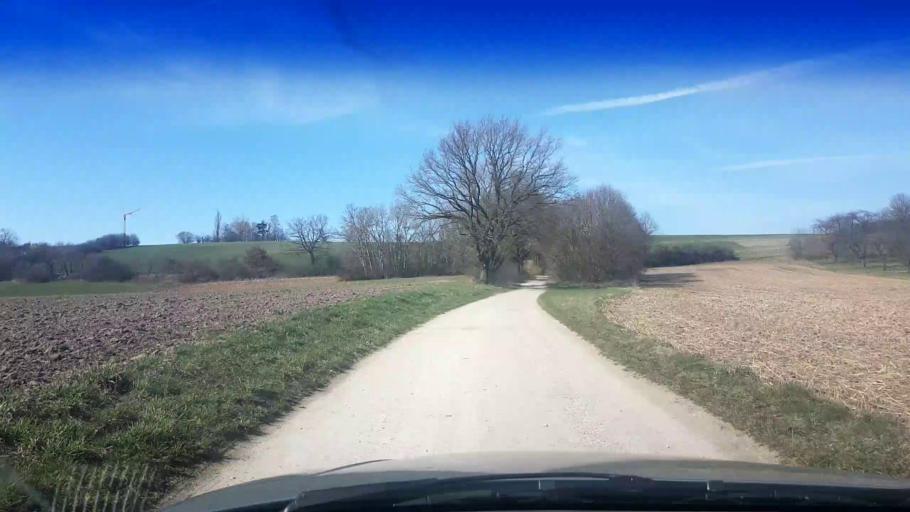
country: DE
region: Bavaria
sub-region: Upper Franconia
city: Bischberg
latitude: 49.8973
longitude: 10.8267
